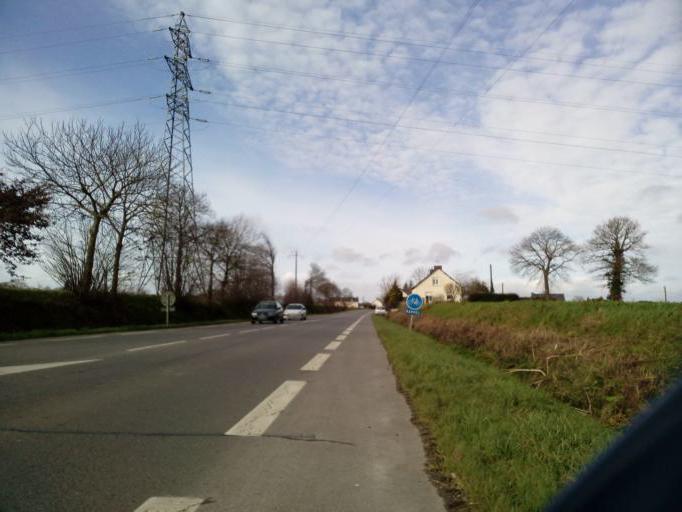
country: FR
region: Brittany
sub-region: Departement d'Ille-et-Vilaine
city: Montgermont
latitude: 48.1666
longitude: -1.7161
